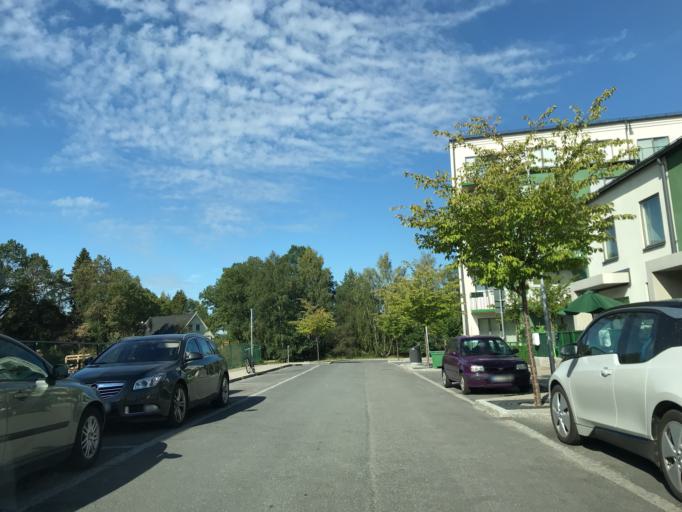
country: SE
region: Stockholm
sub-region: Huddinge Kommun
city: Segeltorp
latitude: 59.2853
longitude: 17.9516
